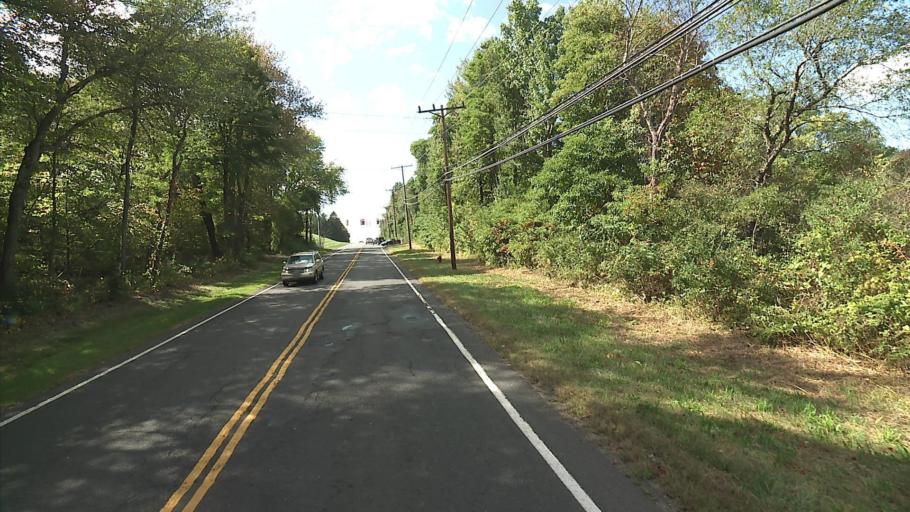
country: US
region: Connecticut
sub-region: Middlesex County
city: Cromwell
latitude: 41.6520
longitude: -72.6618
